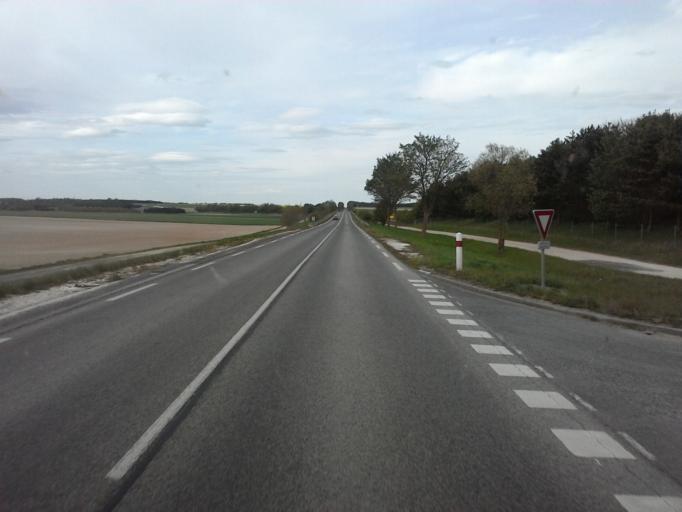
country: FR
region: Champagne-Ardenne
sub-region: Departement de la Marne
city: Compertrix
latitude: 48.8793
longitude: 4.2873
